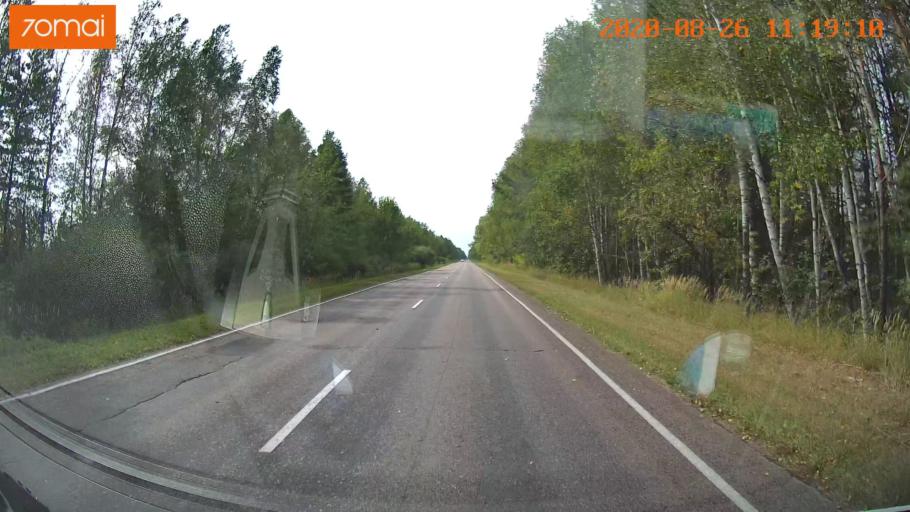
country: RU
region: Rjazan
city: Shilovo
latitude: 54.4023
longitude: 41.0845
